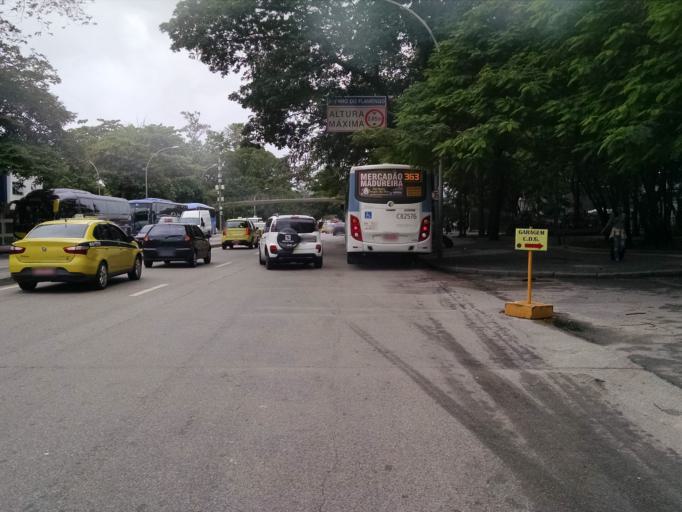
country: BR
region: Rio de Janeiro
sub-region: Rio De Janeiro
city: Rio de Janeiro
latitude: -22.9093
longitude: -43.1684
